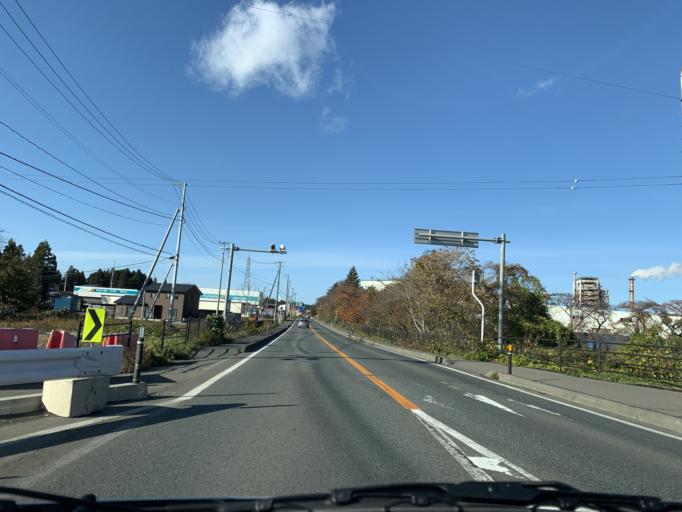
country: JP
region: Iwate
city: Kitakami
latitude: 39.2276
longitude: 141.0939
